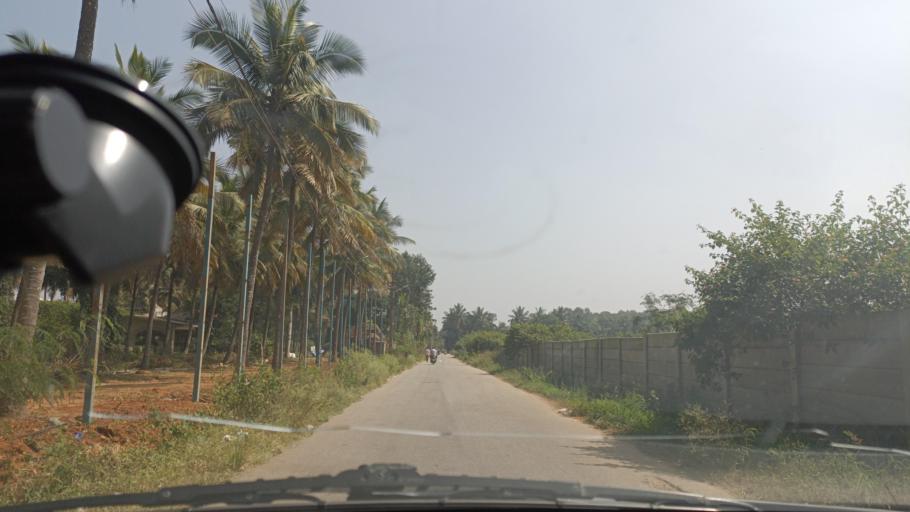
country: IN
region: Karnataka
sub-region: Bangalore Urban
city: Yelahanka
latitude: 13.1169
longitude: 77.6098
